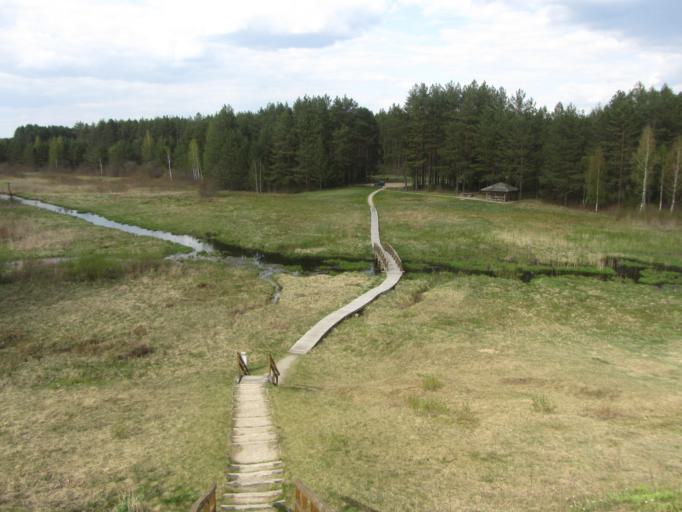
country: LT
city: Salcininkai
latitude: 54.2206
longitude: 25.5989
